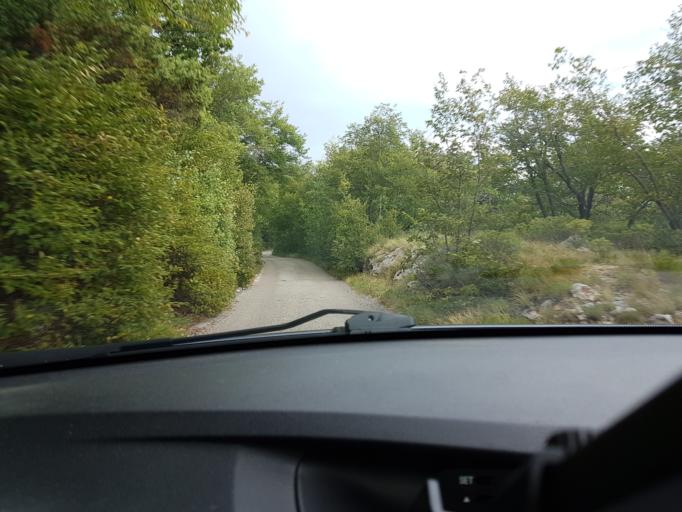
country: HR
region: Primorsko-Goranska
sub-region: Grad Crikvenica
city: Crikvenica
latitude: 45.2326
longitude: 14.7021
